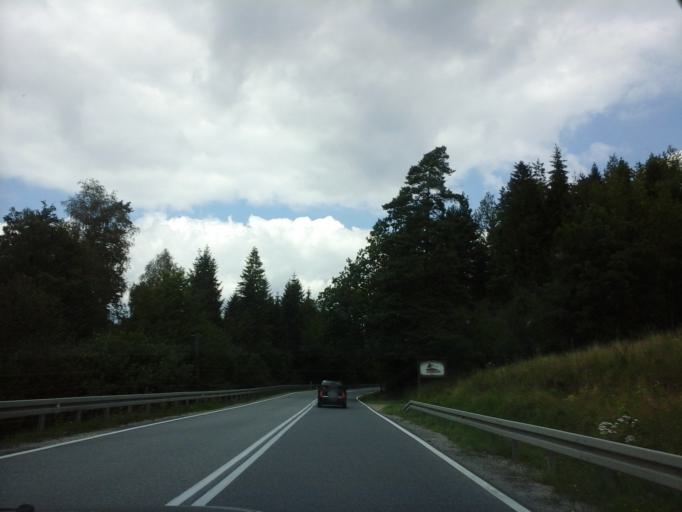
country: PL
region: Lesser Poland Voivodeship
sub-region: Powiat suski
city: Bystra
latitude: 49.6612
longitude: 19.8022
